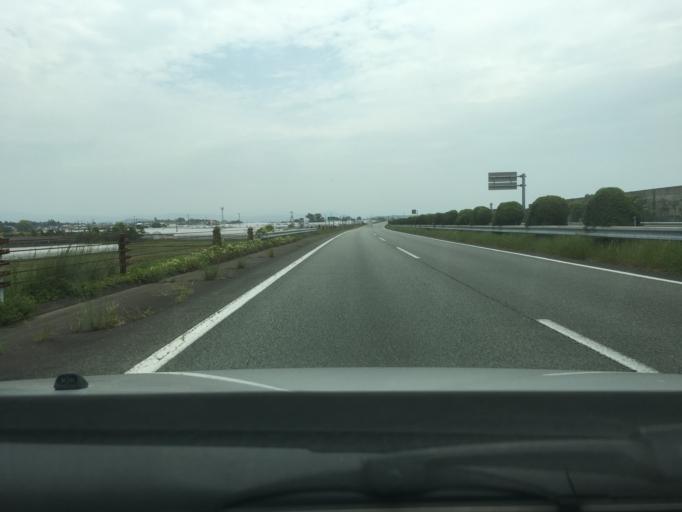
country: JP
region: Kumamoto
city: Ueki
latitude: 32.8860
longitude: 130.7250
